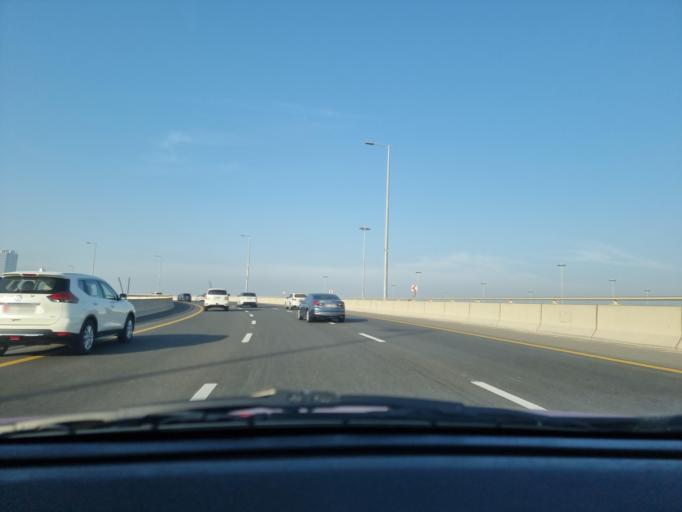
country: AE
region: Abu Dhabi
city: Abu Dhabi
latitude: 24.5154
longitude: 54.3905
